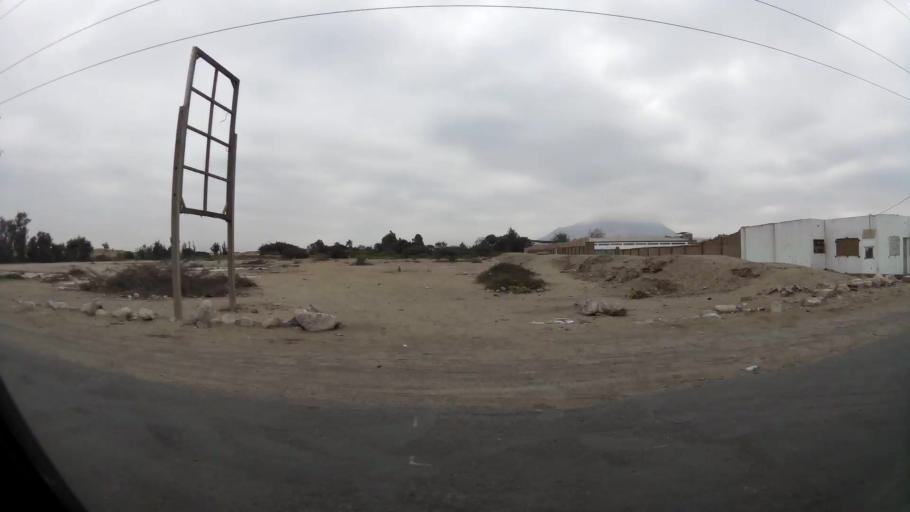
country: PE
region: La Libertad
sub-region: Provincia de Trujillo
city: La Esperanza
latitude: -8.0995
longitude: -79.0653
